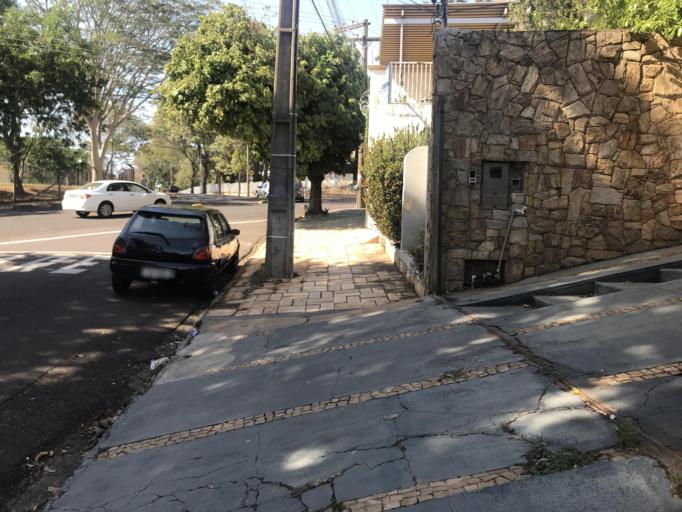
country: BR
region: Sao Paulo
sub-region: Presidente Prudente
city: Presidente Prudente
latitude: -22.1202
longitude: -51.4095
